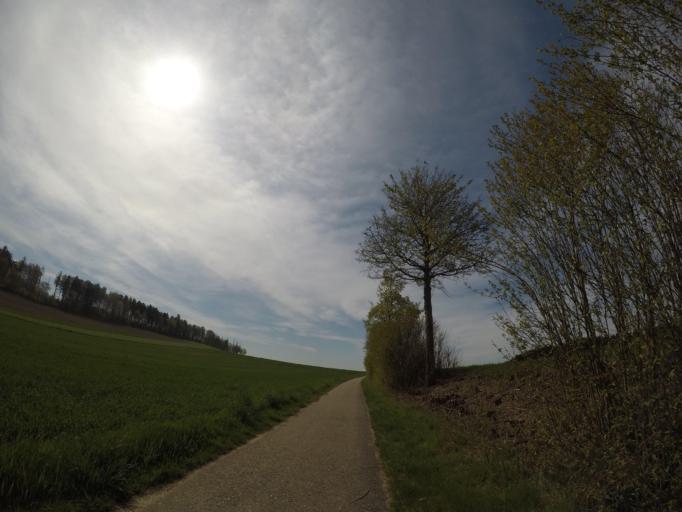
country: DE
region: Baden-Wuerttemberg
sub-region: Tuebingen Region
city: Boms
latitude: 47.9868
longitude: 9.5162
